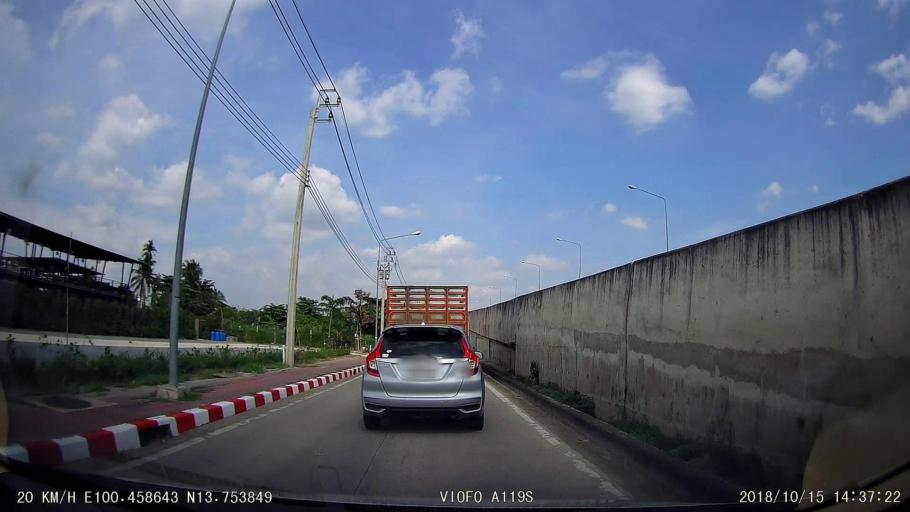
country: TH
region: Bangkok
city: Bangkok Noi
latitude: 13.7539
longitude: 100.4587
